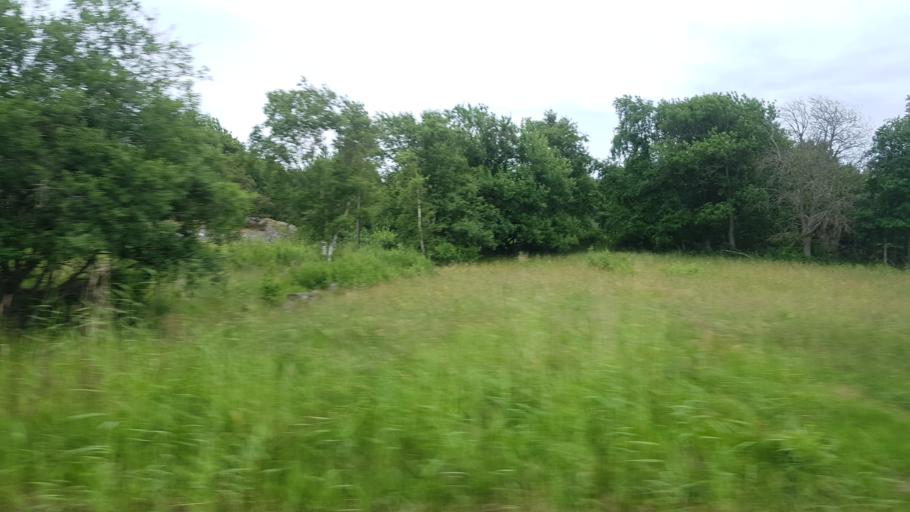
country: SE
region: Vaestra Goetaland
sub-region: Tjorns Kommun
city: Skaerhamn
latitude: 57.9869
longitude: 11.5708
